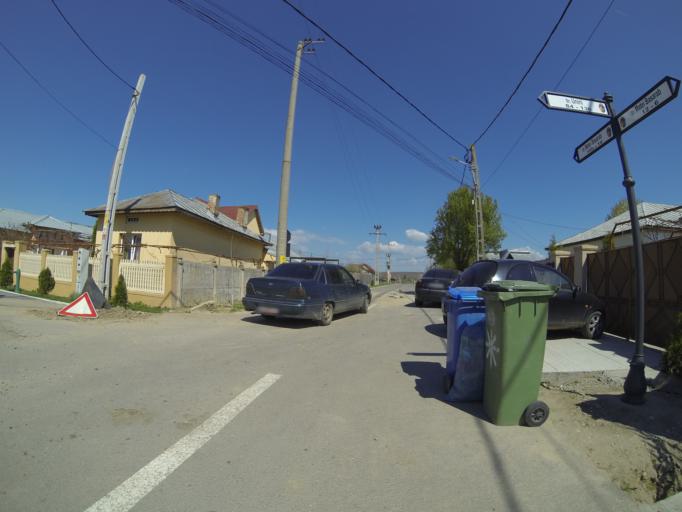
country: RO
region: Dolj
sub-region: Comuna Isalnita
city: Isalnita
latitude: 44.3941
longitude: 23.7477
